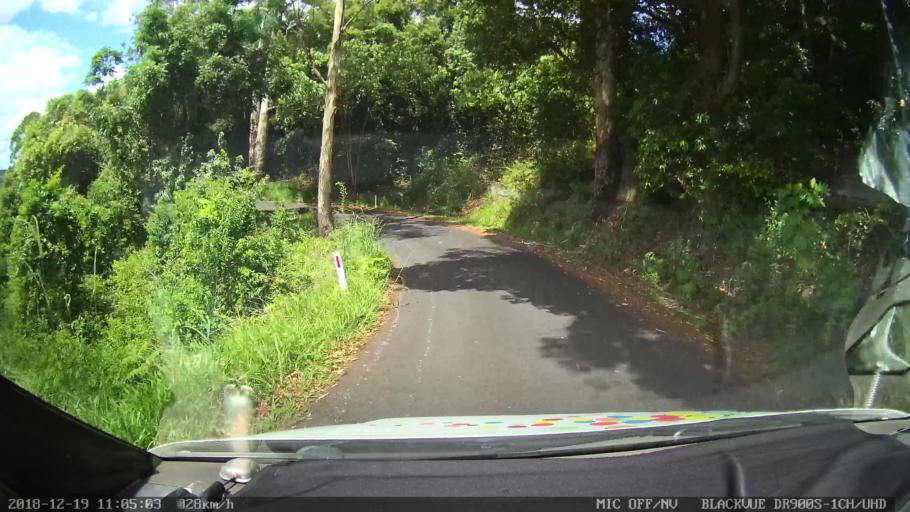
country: AU
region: New South Wales
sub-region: Lismore Municipality
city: Nimbin
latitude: -28.6156
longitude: 153.2653
